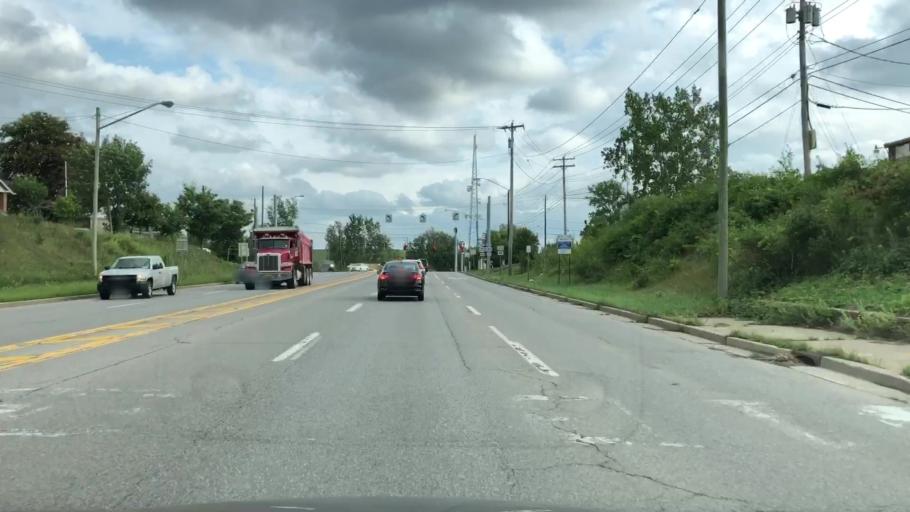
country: US
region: New York
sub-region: Erie County
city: Cheektowaga
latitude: 42.9066
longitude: -78.7284
